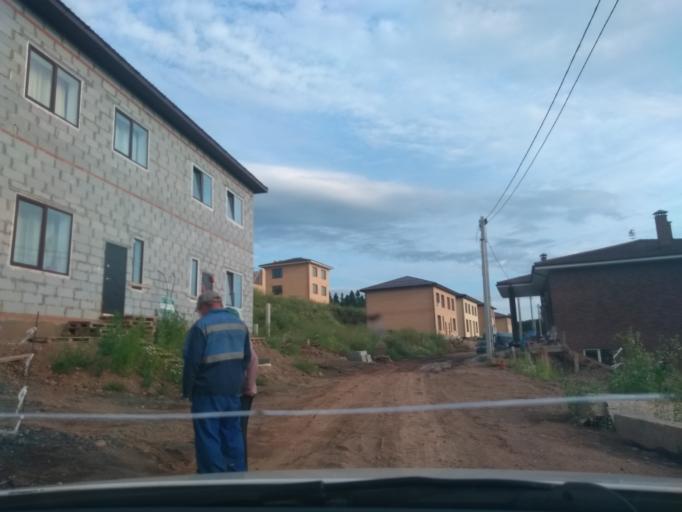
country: RU
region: Perm
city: Perm
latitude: 58.0001
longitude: 56.3214
